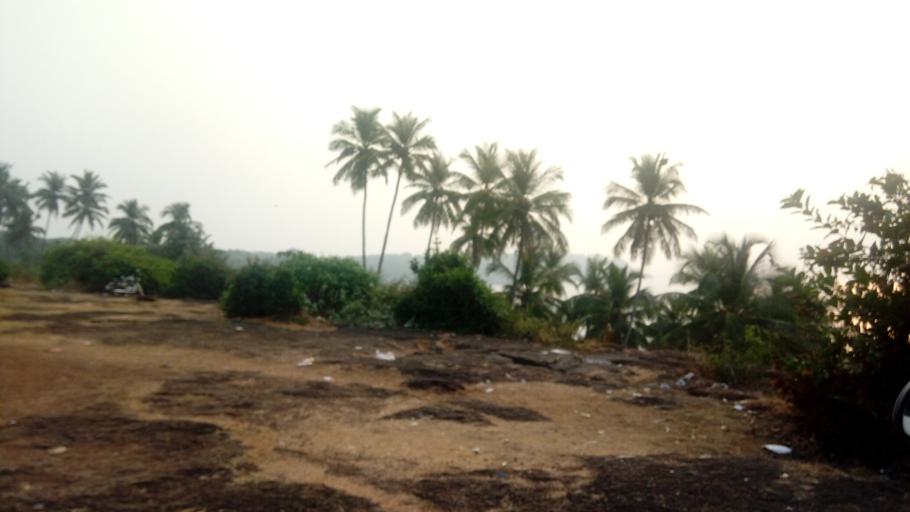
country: IN
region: Goa
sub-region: South Goa
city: Cavelossim
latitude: 15.1002
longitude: 73.9269
